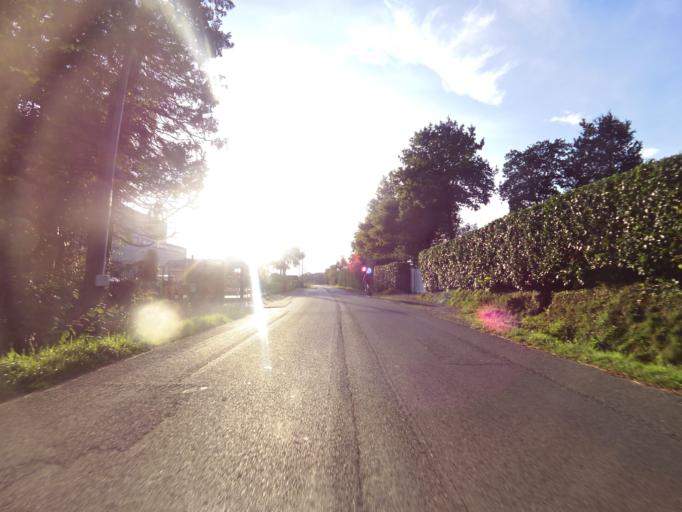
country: FR
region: Brittany
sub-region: Departement du Morbihan
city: Questembert
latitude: 47.6650
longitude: -2.4857
